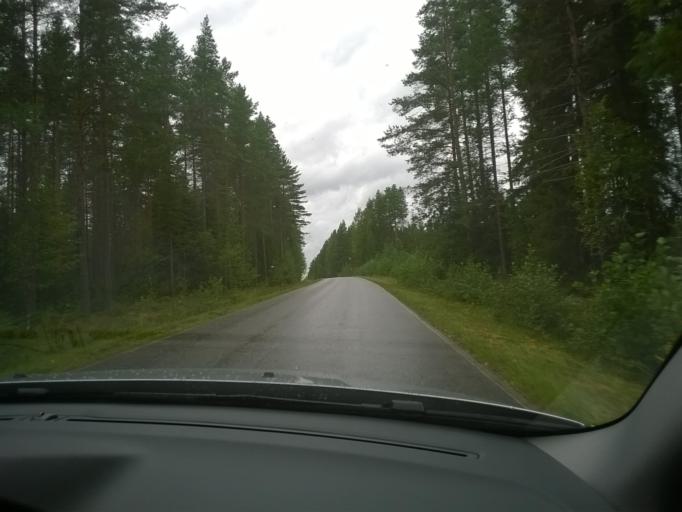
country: FI
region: Kainuu
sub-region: Kehys-Kainuu
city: Kuhmo
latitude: 64.1329
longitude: 29.4382
